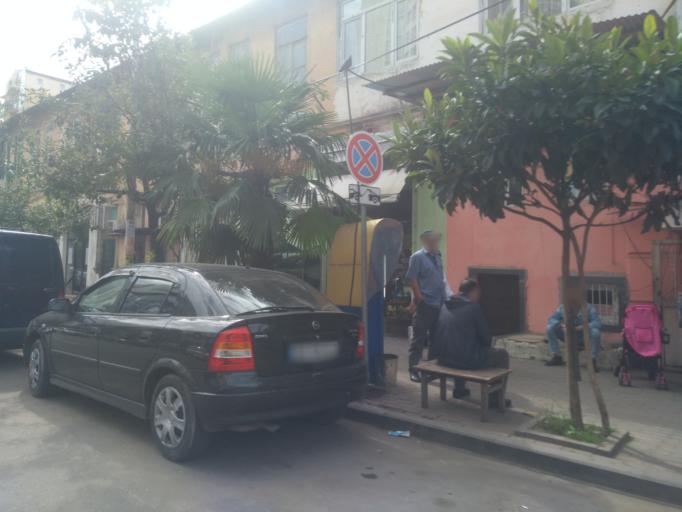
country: GE
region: Ajaria
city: Batumi
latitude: 41.6405
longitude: 41.6274
